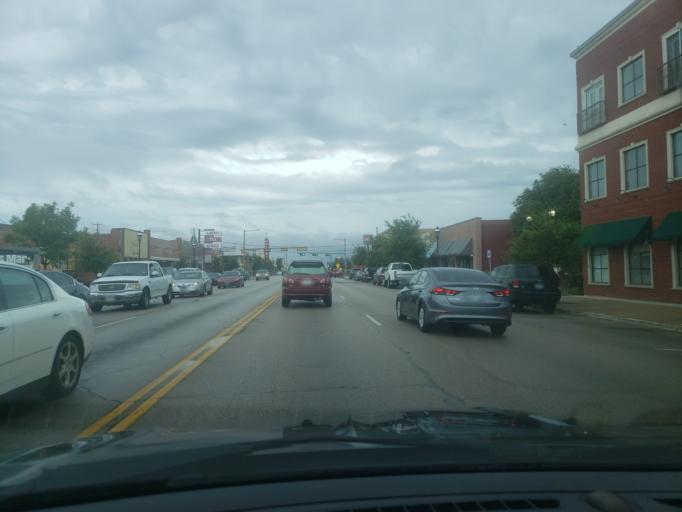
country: US
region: Texas
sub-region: Dallas County
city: Grand Prairie
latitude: 32.7454
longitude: -97.0049
